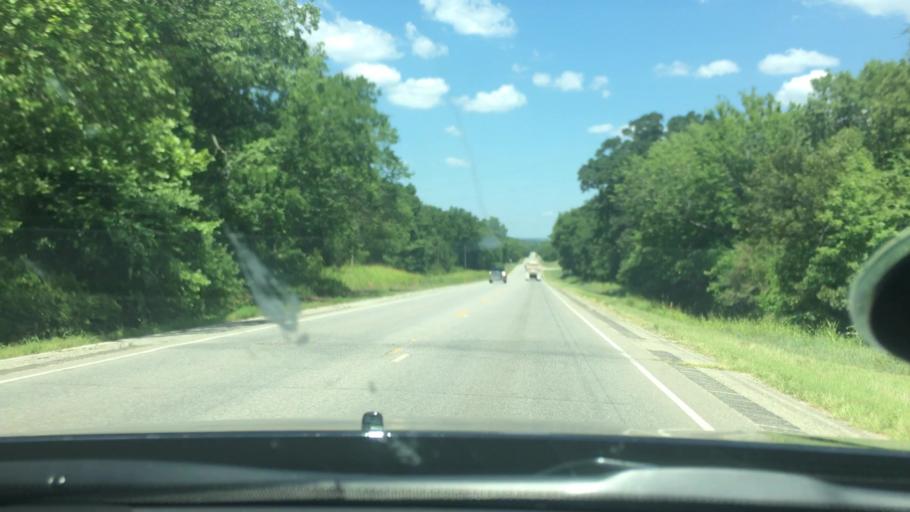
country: US
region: Oklahoma
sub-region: Marshall County
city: Oakland
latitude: 34.1582
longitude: -96.8214
